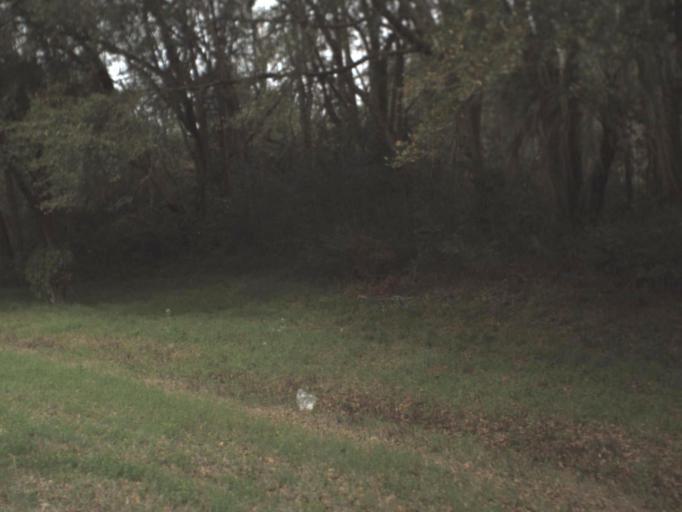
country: US
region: Florida
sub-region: Jefferson County
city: Monticello
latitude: 30.5240
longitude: -84.0219
